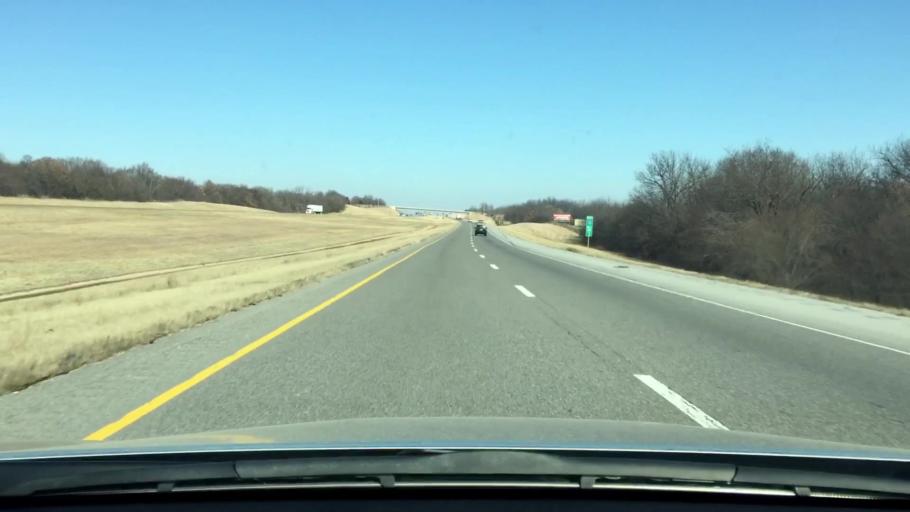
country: US
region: Oklahoma
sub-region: McClain County
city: Purcell
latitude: 34.9496
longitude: -97.3684
